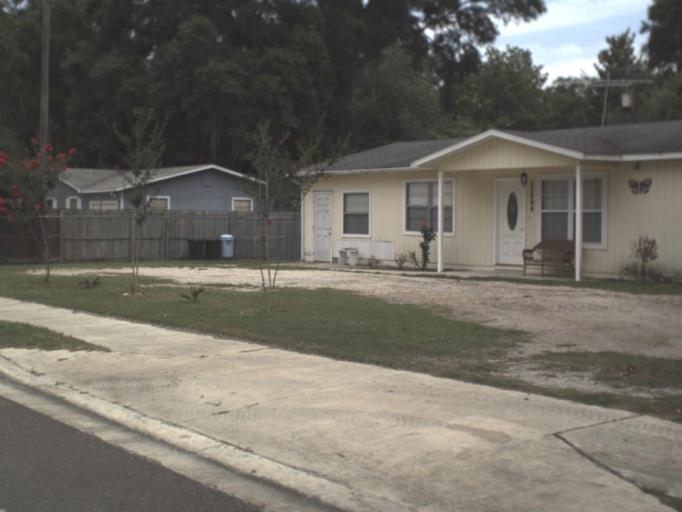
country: US
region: Florida
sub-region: Alachua County
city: Hawthorne
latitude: 29.5965
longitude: -82.0804
